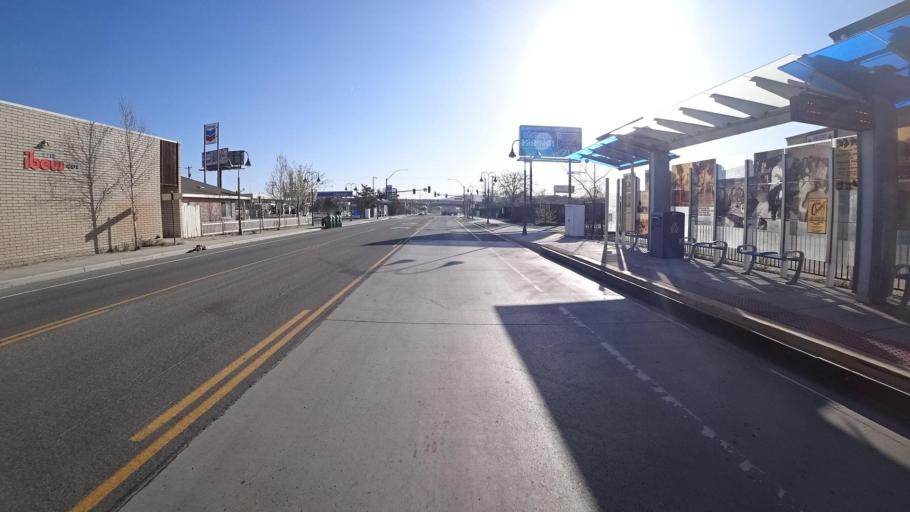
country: US
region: Nevada
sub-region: Washoe County
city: Sparks
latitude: 39.5349
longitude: -119.7819
